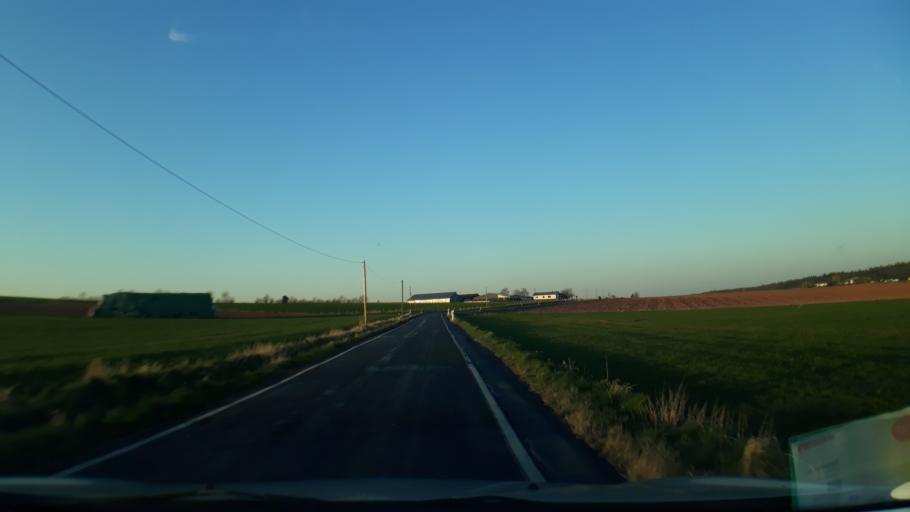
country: DE
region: North Rhine-Westphalia
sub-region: Regierungsbezirk Koln
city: Mechernich
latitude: 50.6127
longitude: 6.5978
